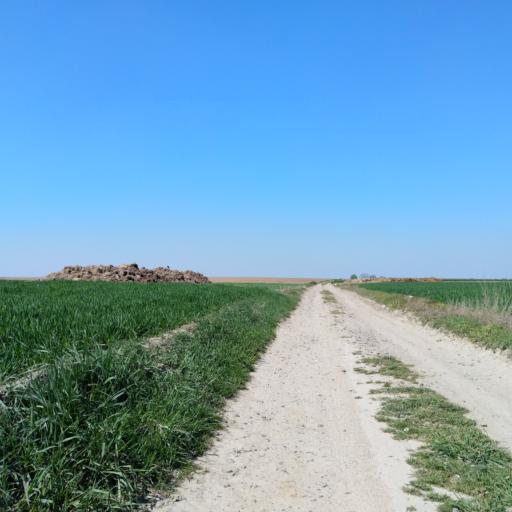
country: BE
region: Wallonia
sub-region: Province du Hainaut
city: Lens
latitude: 50.5723
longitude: 3.8848
